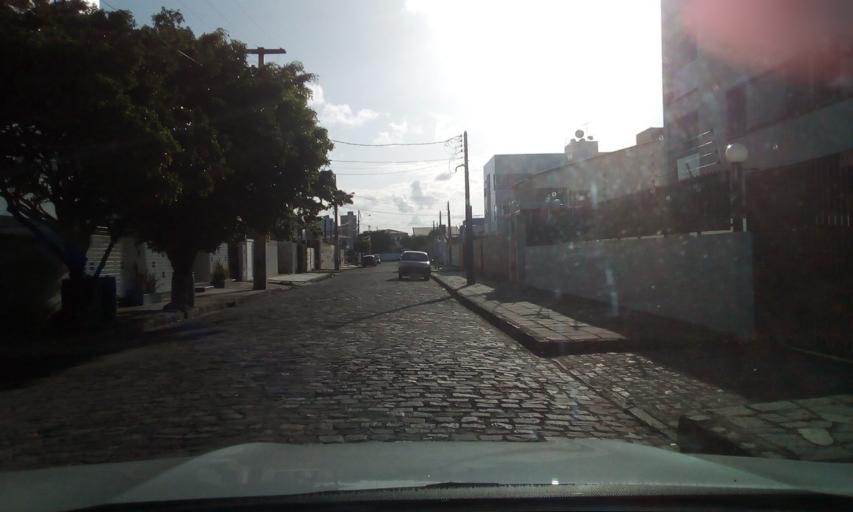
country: BR
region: Paraiba
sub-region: Joao Pessoa
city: Joao Pessoa
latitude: -7.0933
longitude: -34.8360
